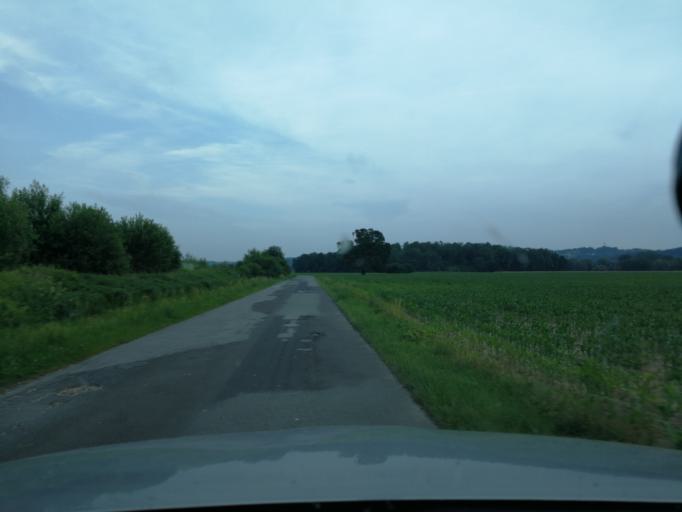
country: AT
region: Burgenland
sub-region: Politischer Bezirk Jennersdorf
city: Konigsdorf
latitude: 47.0122
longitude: 16.1551
